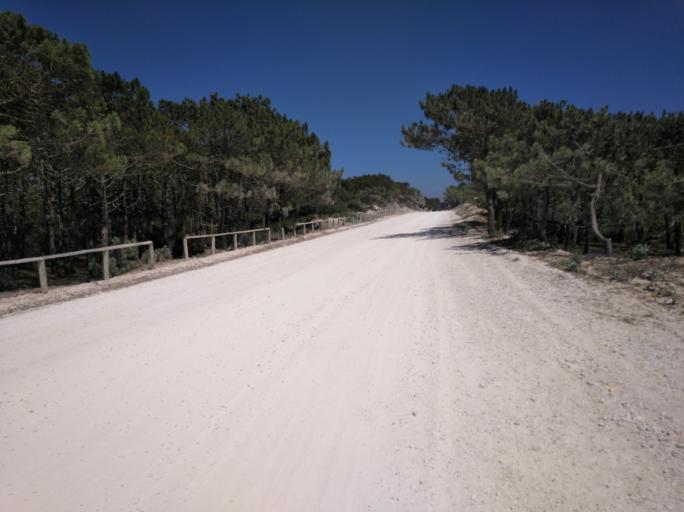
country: PT
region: Coimbra
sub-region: Figueira da Foz
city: Lavos
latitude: 40.0025
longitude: -8.9109
